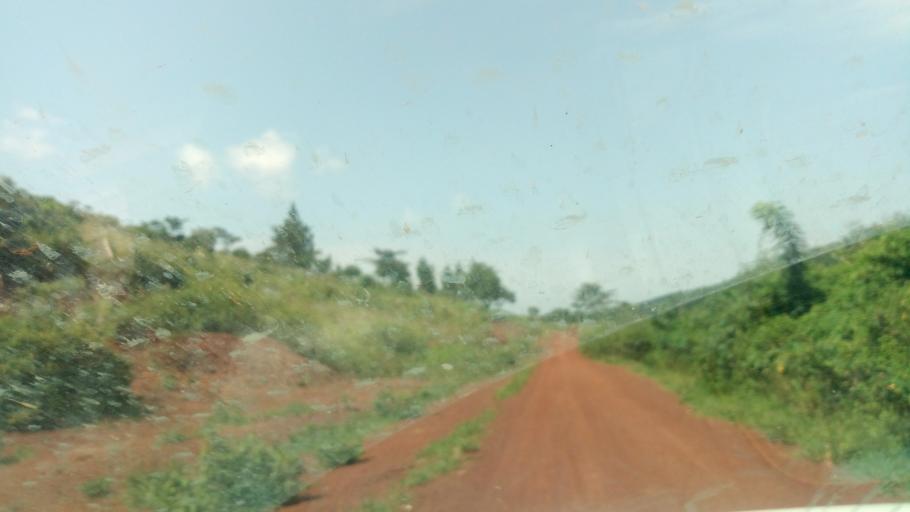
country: UG
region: Western Region
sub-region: Masindi District
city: Masindi
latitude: 1.6490
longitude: 31.8062
